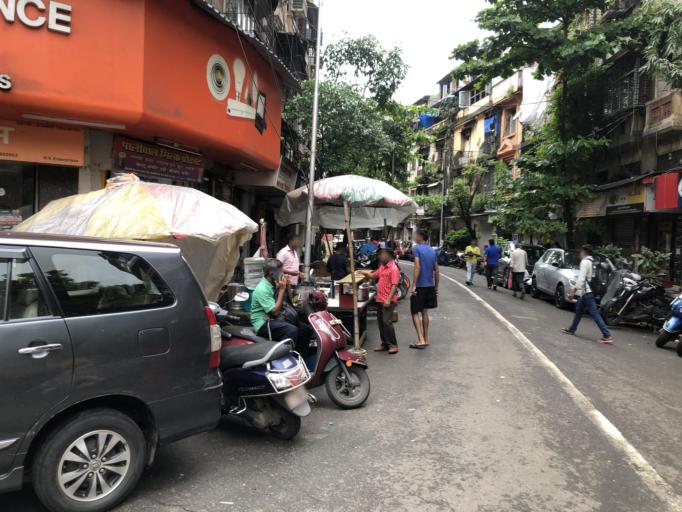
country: IN
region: Maharashtra
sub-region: Raigarh
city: Uran
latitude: 18.9456
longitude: 72.8292
